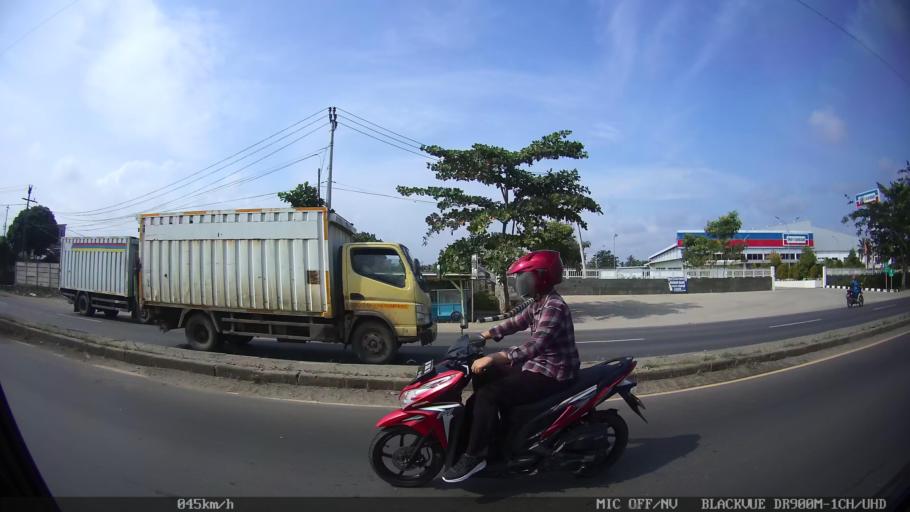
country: ID
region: Lampung
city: Kedaton
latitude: -5.3586
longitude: 105.2505
